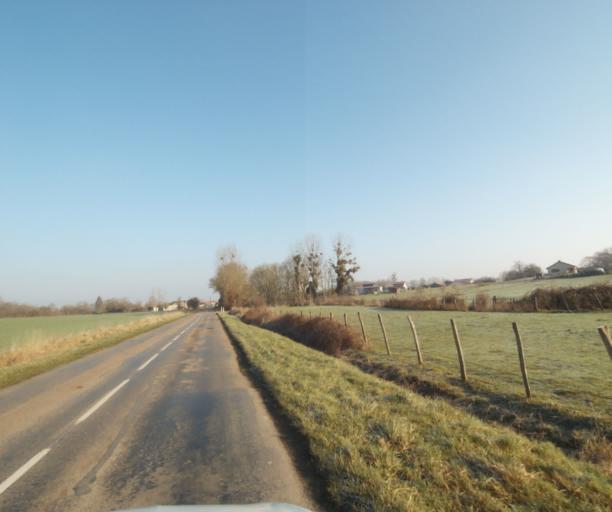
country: FR
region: Champagne-Ardenne
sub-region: Departement de la Haute-Marne
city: Montier-en-Der
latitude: 48.4505
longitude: 4.7656
